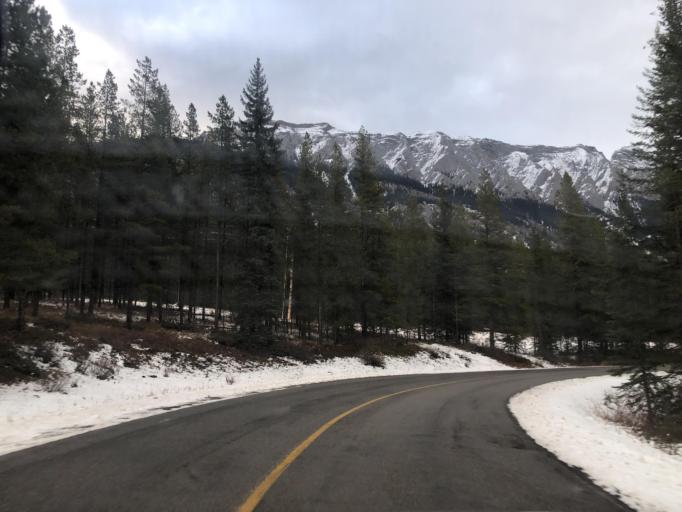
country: CA
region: Alberta
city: Canmore
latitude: 50.7106
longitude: -115.1146
